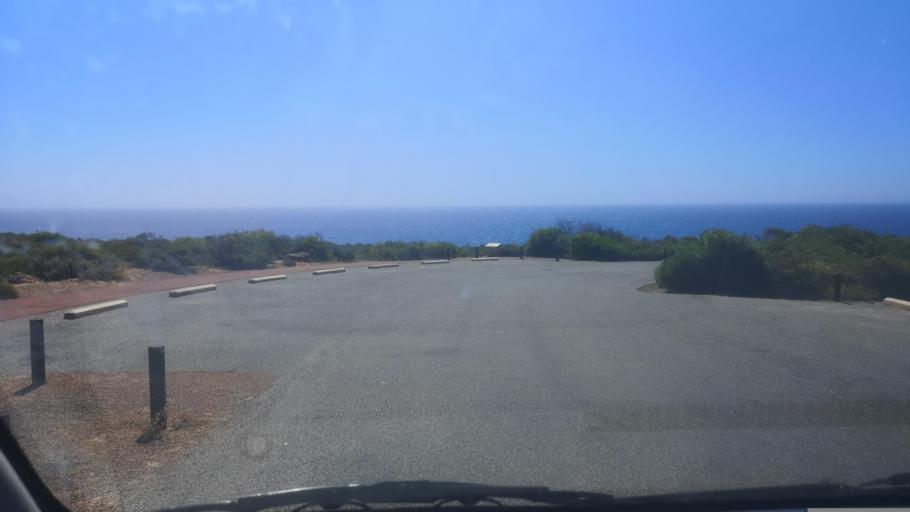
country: AU
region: Western Australia
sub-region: Northampton Shire
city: Kalbarri
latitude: -27.8276
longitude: 114.1134
